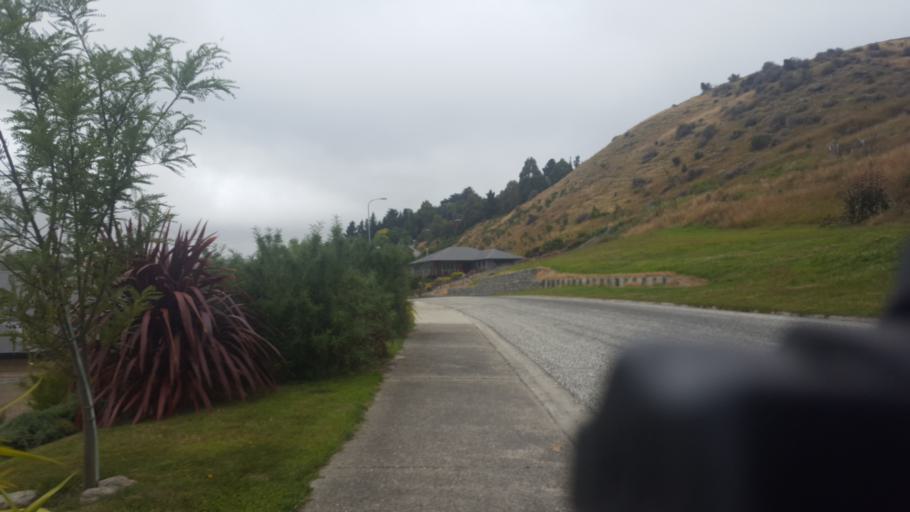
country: NZ
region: Otago
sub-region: Queenstown-Lakes District
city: Kingston
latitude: -45.5338
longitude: 169.3004
